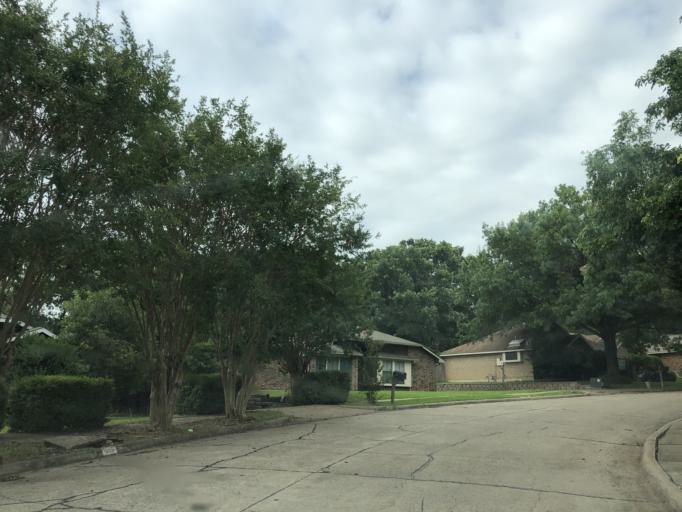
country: US
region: Texas
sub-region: Dallas County
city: Sunnyvale
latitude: 32.8459
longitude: -96.6091
